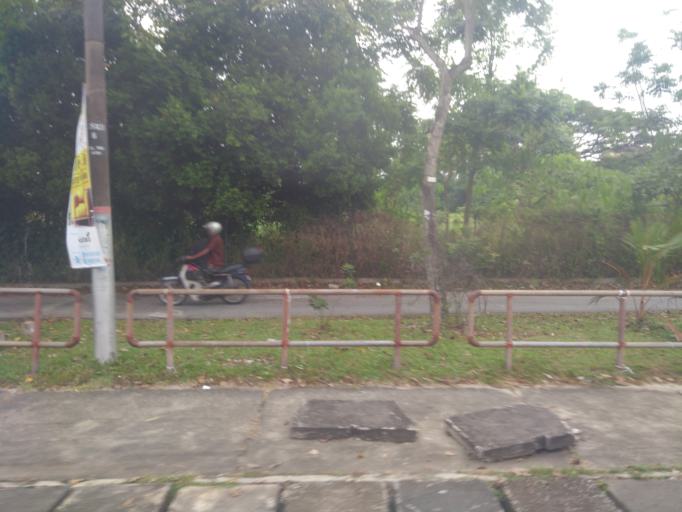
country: MY
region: Johor
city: Johor Bahru
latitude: 1.4925
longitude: 103.7070
